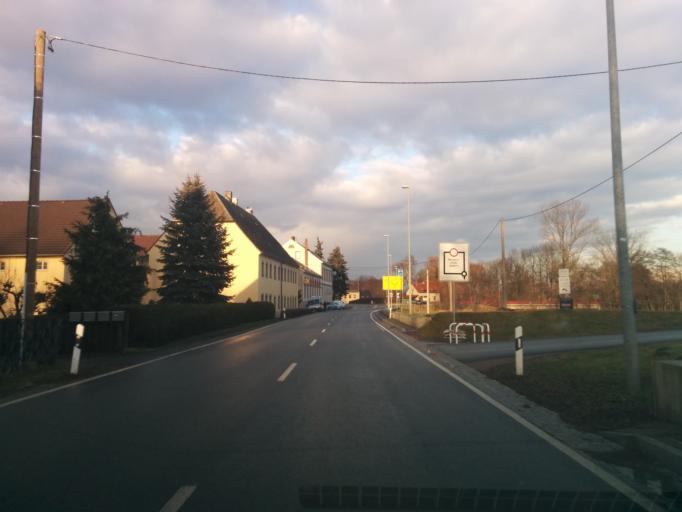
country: DE
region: Saxony
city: Niederwiesa
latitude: 50.8992
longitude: 13.0096
